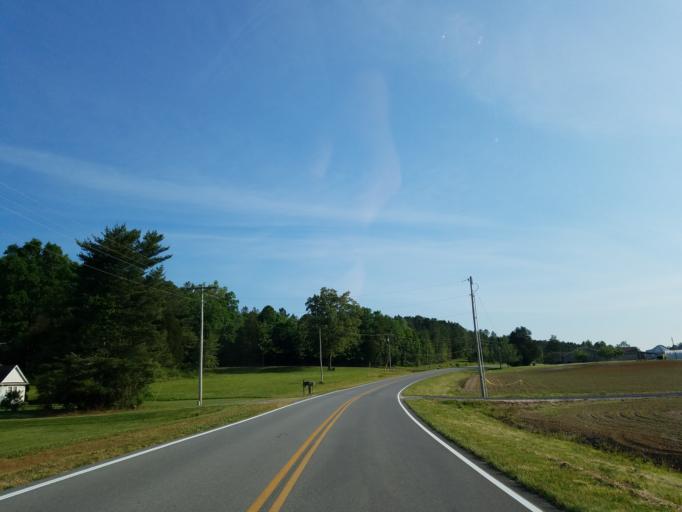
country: US
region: Georgia
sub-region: Chattooga County
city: Trion
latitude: 34.5137
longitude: -85.2310
